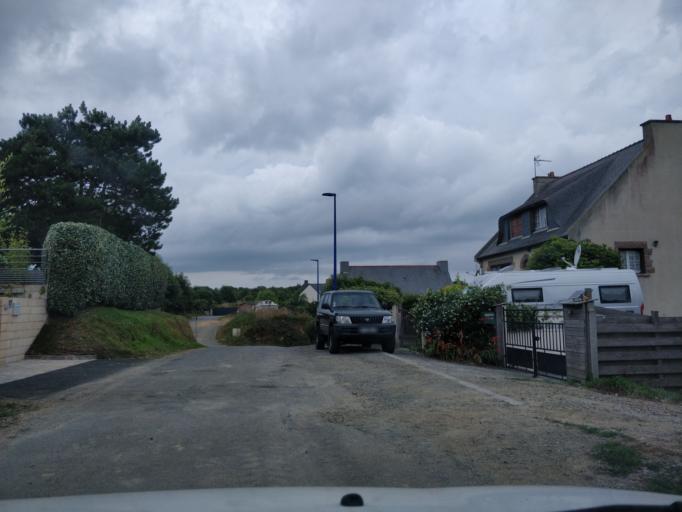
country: FR
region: Brittany
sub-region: Departement des Cotes-d'Armor
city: Louannec
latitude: 48.7942
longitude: -3.4185
